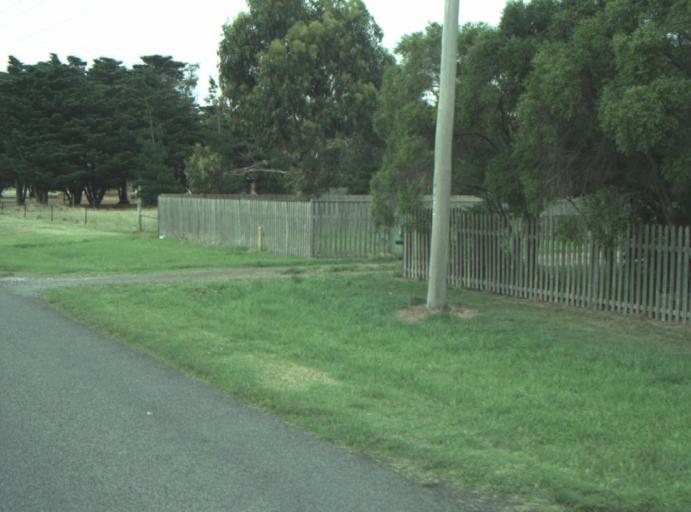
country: AU
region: Victoria
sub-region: Greater Geelong
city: Bell Post Hill
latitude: -38.0432
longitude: 144.3089
